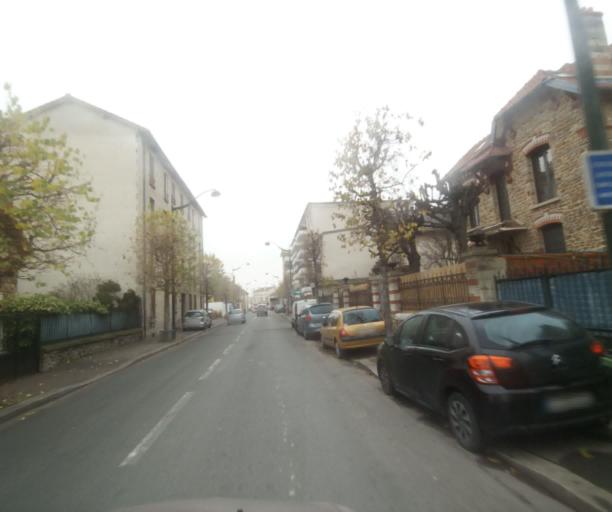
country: FR
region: Ile-de-France
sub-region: Departement de Seine-Saint-Denis
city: Bondy
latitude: 48.9073
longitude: 2.4970
